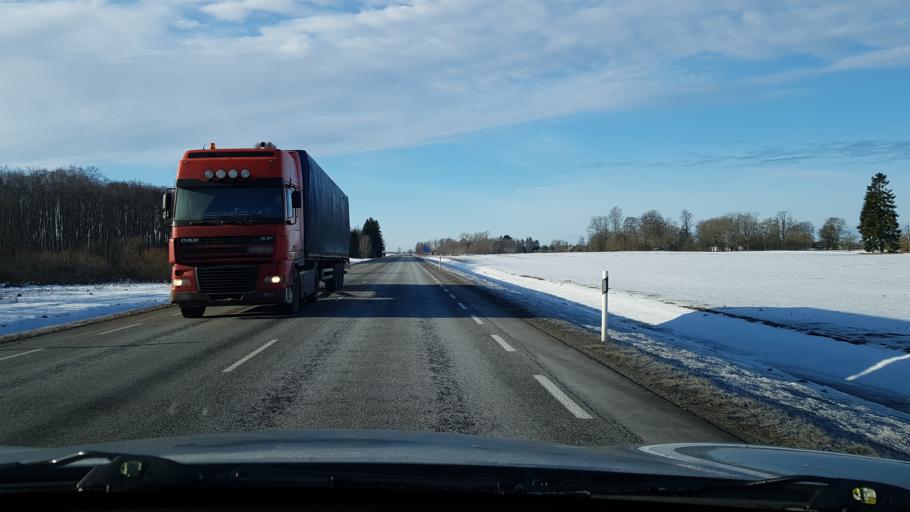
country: EE
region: Viljandimaa
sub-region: Vohma linn
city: Vohma
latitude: 58.6621
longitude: 25.6198
